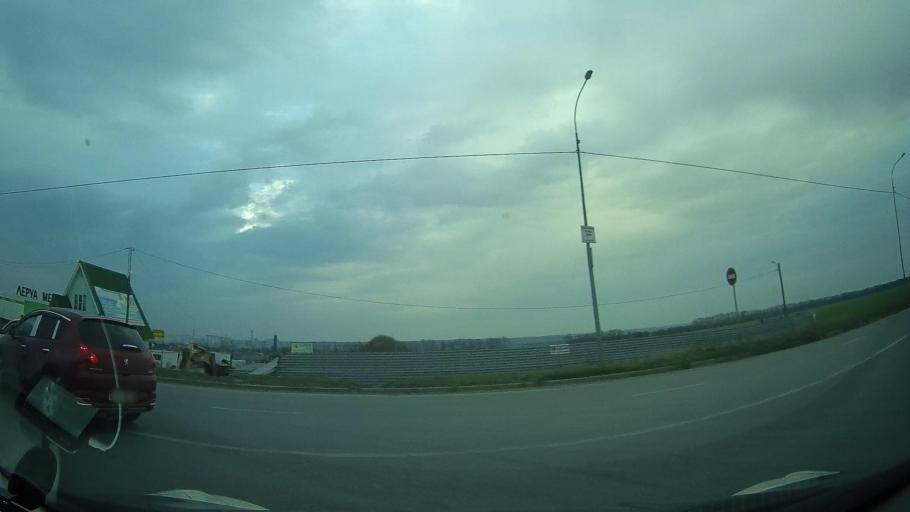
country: RU
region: Rostov
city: Temernik
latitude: 47.3103
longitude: 39.7293
